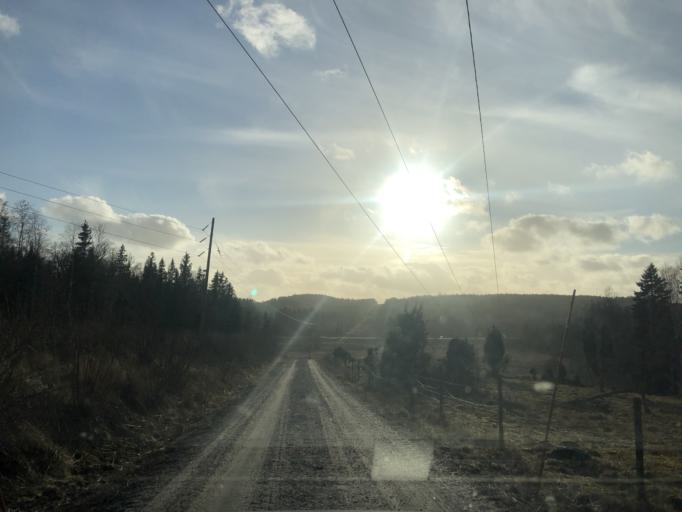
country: SE
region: Vaestra Goetaland
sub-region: Ulricehamns Kommun
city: Ulricehamn
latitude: 57.8178
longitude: 13.3623
